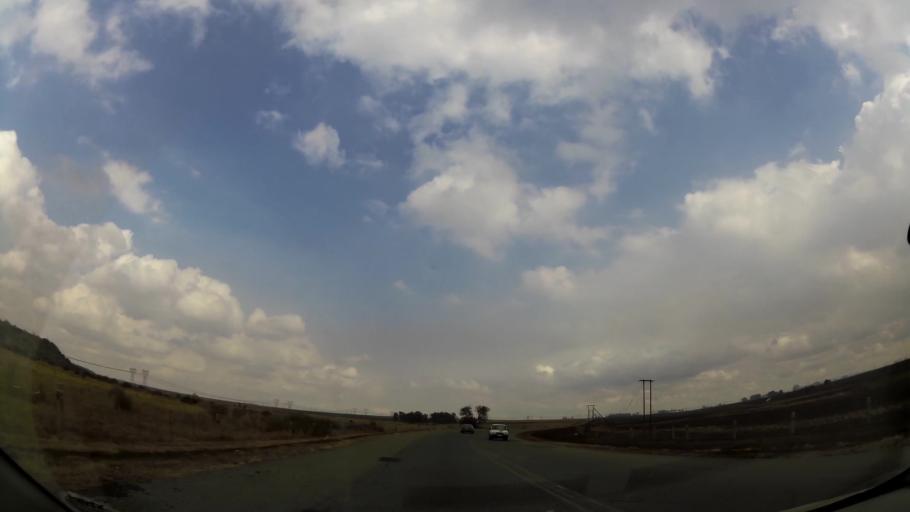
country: ZA
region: Orange Free State
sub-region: Fezile Dabi District Municipality
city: Sasolburg
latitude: -26.8065
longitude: 27.9127
